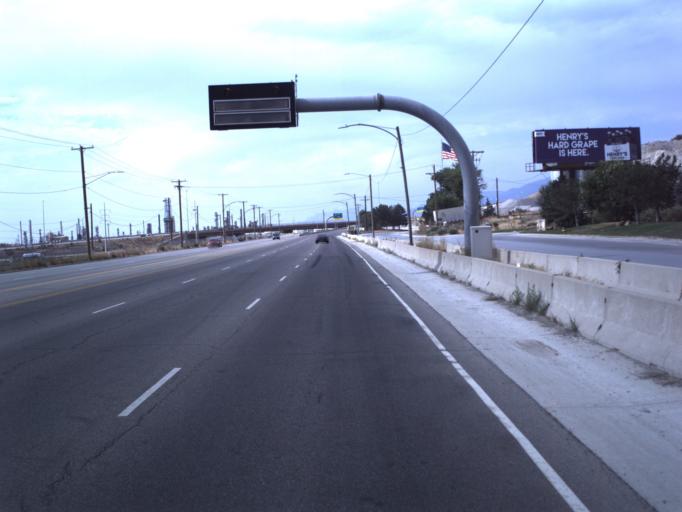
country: US
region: Utah
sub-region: Davis County
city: North Salt Lake
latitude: 40.8093
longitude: -111.9184
